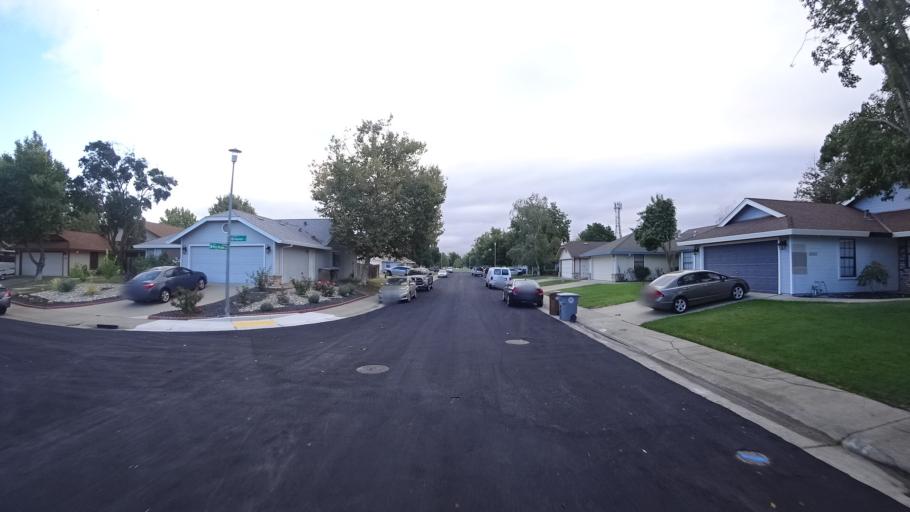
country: US
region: California
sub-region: Sacramento County
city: Laguna
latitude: 38.4273
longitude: -121.4445
